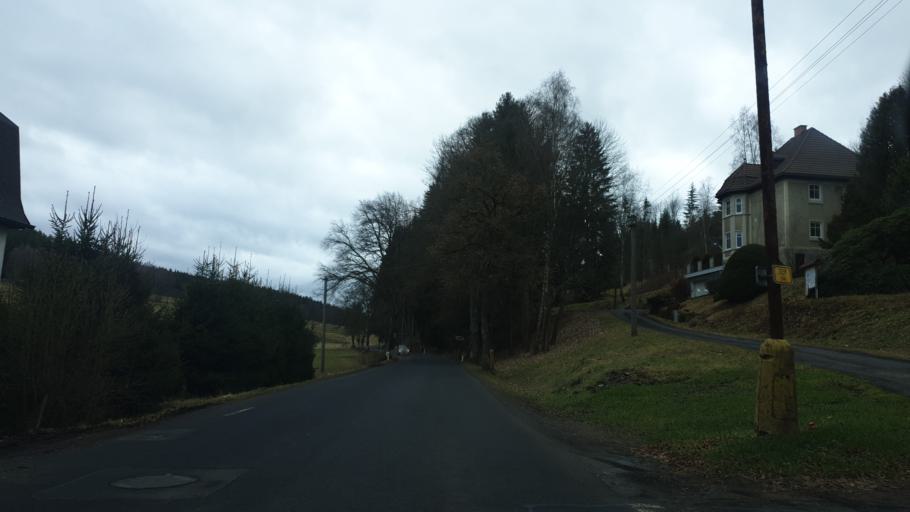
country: CZ
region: Karlovarsky
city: As
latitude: 50.2547
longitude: 12.2011
